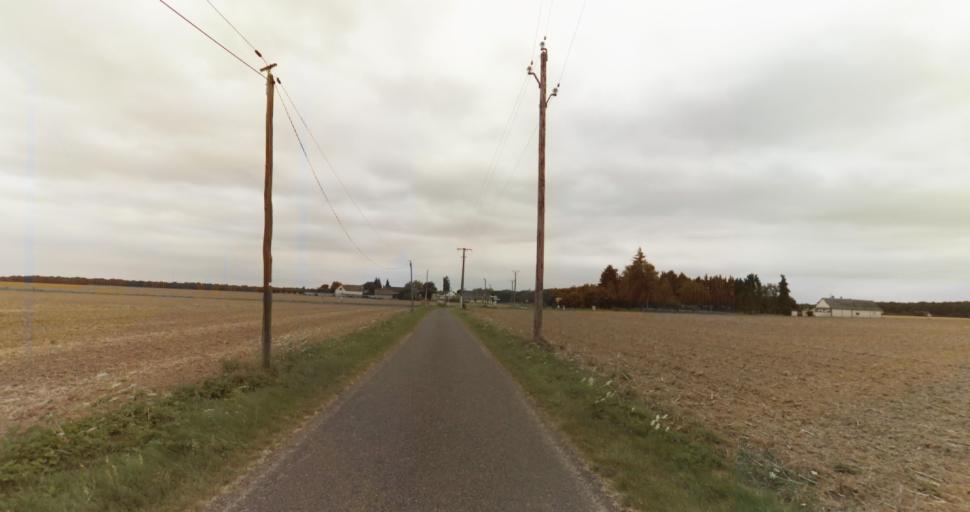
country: FR
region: Haute-Normandie
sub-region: Departement de l'Eure
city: La Couture-Boussey
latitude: 48.9124
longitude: 1.3153
